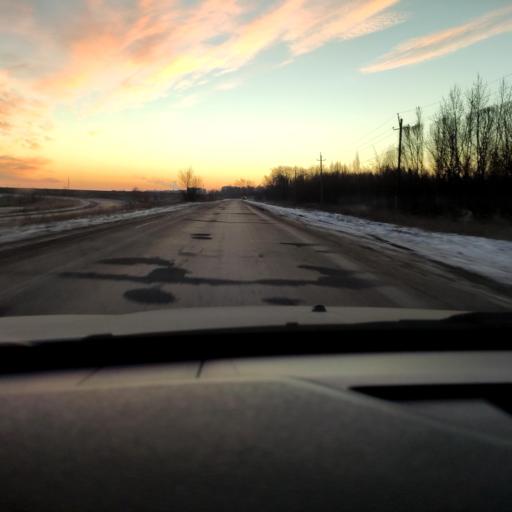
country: RU
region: Samara
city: Smyshlyayevka
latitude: 53.2592
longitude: 50.4704
